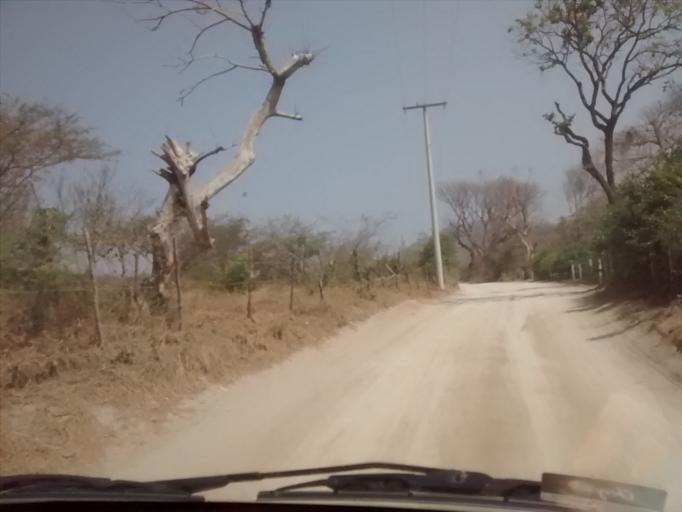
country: CO
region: Magdalena
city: Santa Marta
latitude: 11.1655
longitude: -74.2146
